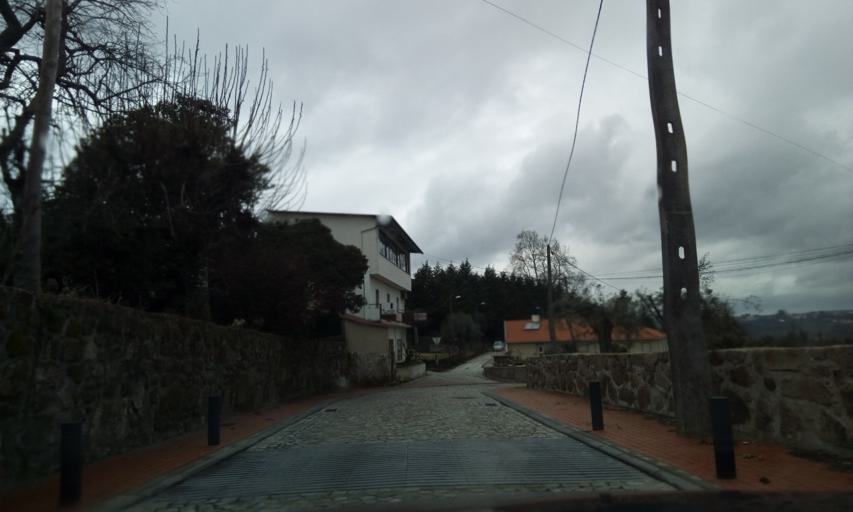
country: PT
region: Viseu
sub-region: Nelas
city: Nelas
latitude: 40.6007
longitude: -7.8448
